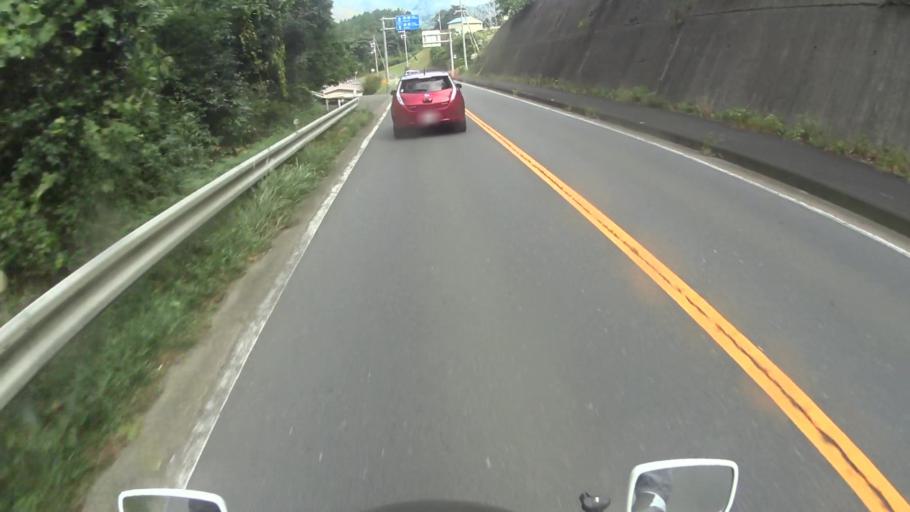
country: JP
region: Kyoto
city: Ayabe
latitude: 35.2508
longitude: 135.4177
